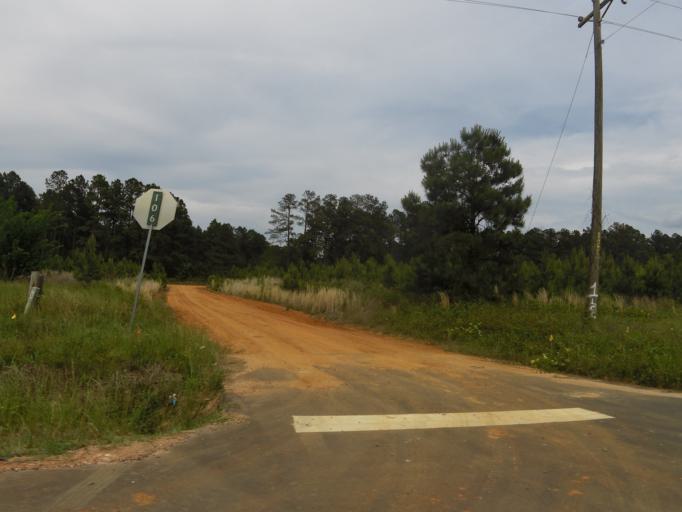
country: US
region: Georgia
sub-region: Jefferson County
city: Wrens
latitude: 33.3104
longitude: -82.4457
